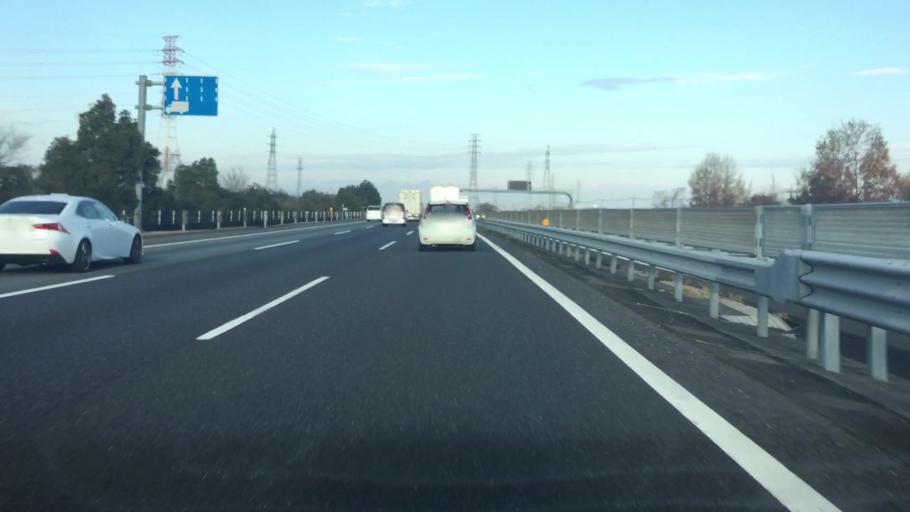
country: JP
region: Saitama
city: Honjo
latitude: 36.2221
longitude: 139.1615
